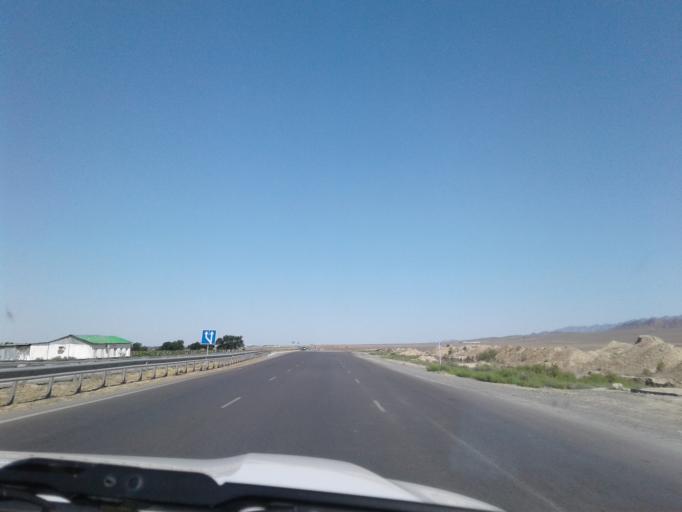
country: TM
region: Ahal
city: Annau
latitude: 37.7863
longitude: 58.8370
